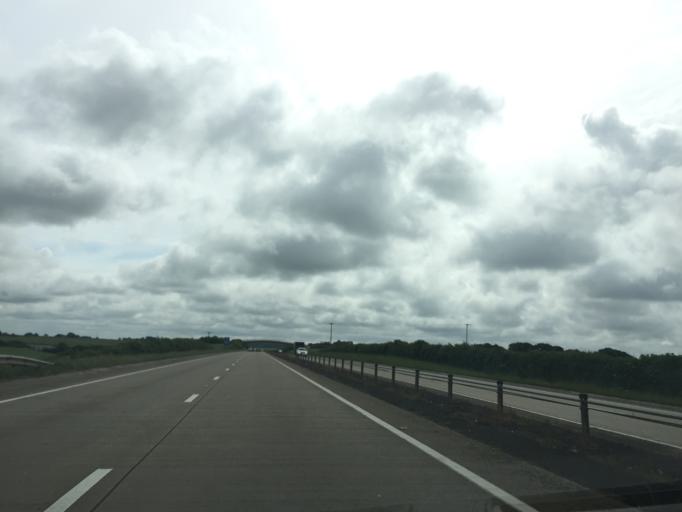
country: GB
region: England
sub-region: Dorset
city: Bovington Camp
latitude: 50.7538
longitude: -2.2973
